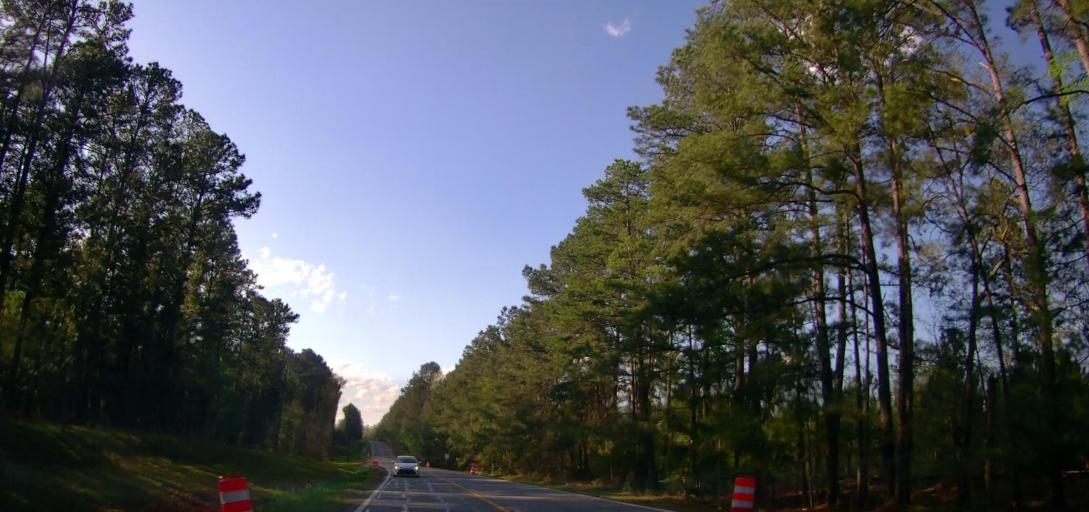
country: US
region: Georgia
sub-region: Baldwin County
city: Milledgeville
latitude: 33.1170
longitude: -83.2880
